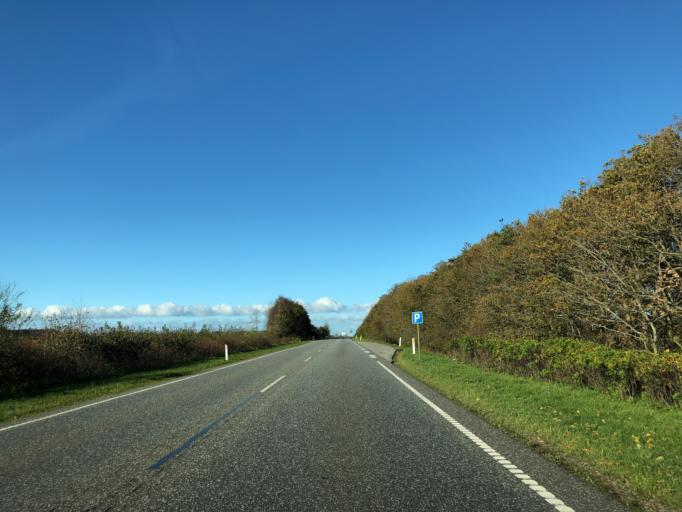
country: DK
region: Central Jutland
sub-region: Herning Kommune
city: Avlum
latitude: 56.2970
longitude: 8.7218
